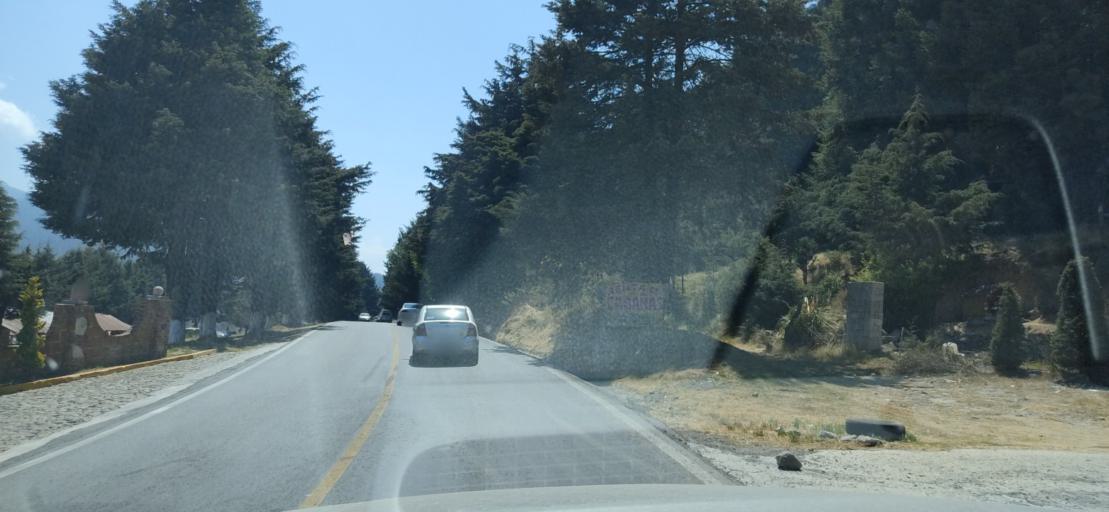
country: MX
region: Mexico
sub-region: Ocoyoacac
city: San Jeronimo Acazulco
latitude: 19.2891
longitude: -99.3740
